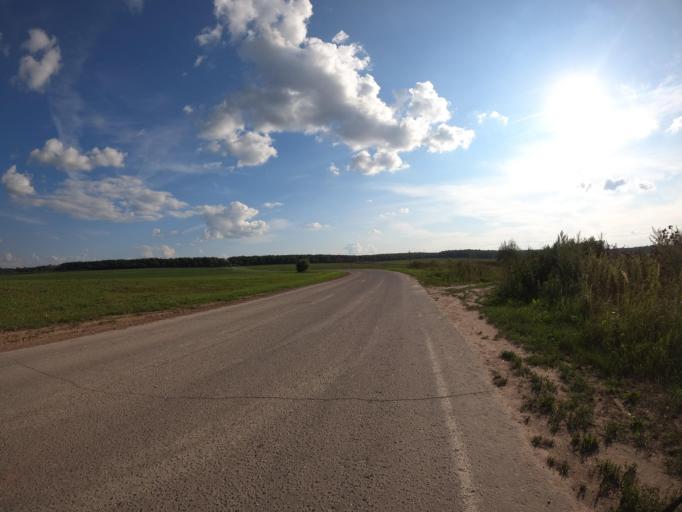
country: RU
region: Moskovskaya
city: Meshcherino
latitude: 55.1889
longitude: 38.4731
